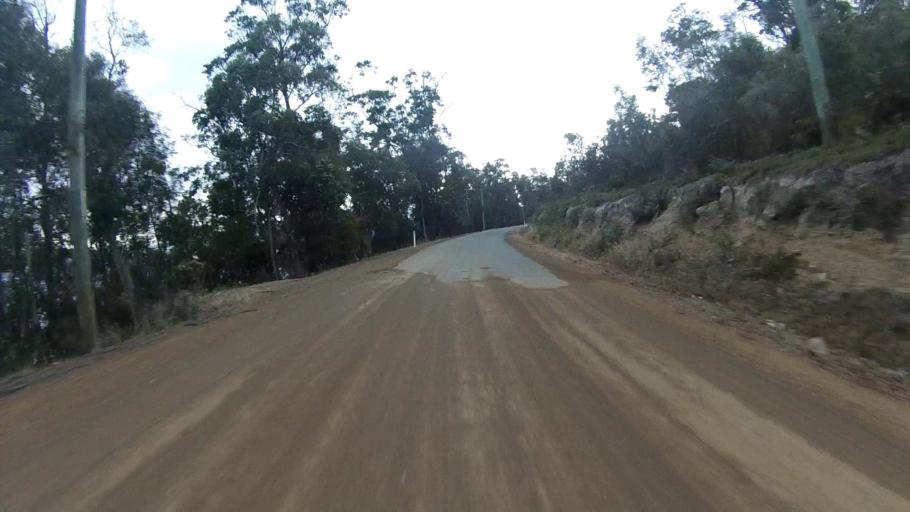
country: AU
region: Tasmania
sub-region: Huon Valley
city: Cygnet
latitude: -43.2197
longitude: 147.0923
